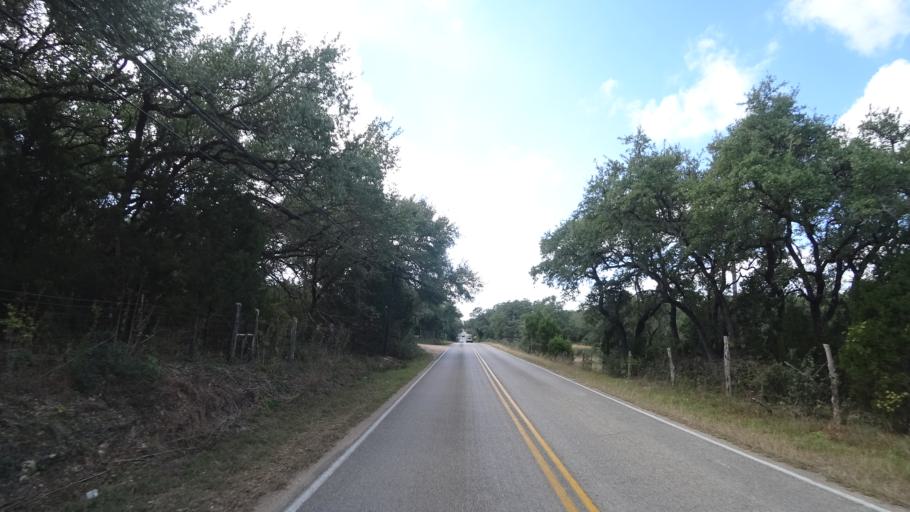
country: US
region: Texas
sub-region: Travis County
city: Barton Creek
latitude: 30.2541
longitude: -97.9171
